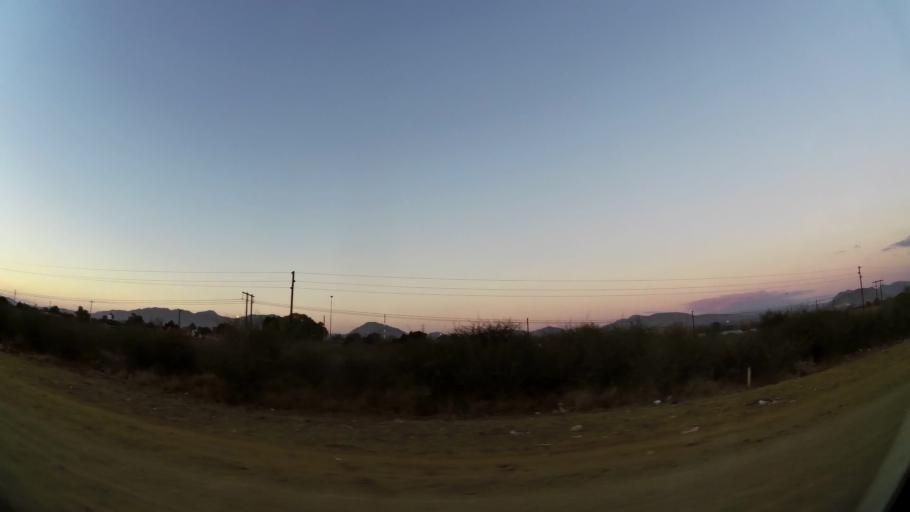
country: ZA
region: Limpopo
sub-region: Waterberg District Municipality
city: Mokopane
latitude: -24.1515
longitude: 28.9752
